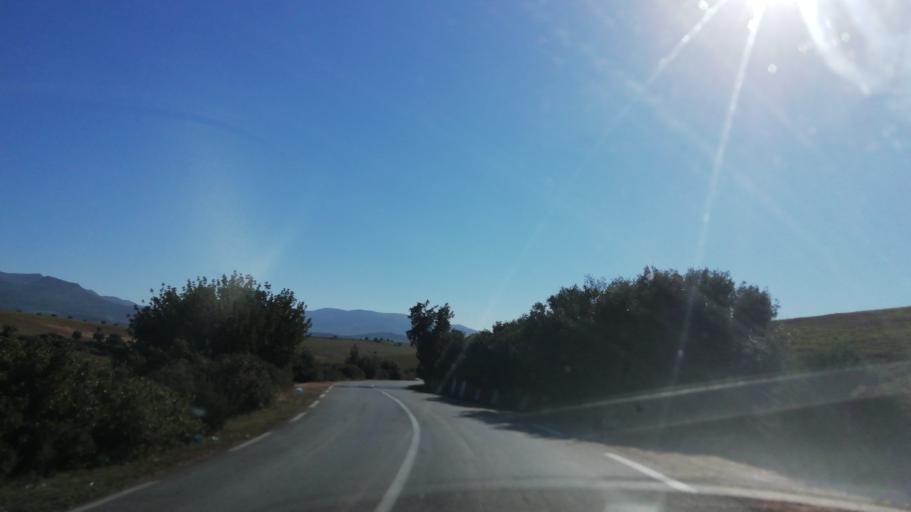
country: DZ
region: Tlemcen
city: Beni Mester
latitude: 34.8277
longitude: -1.5870
